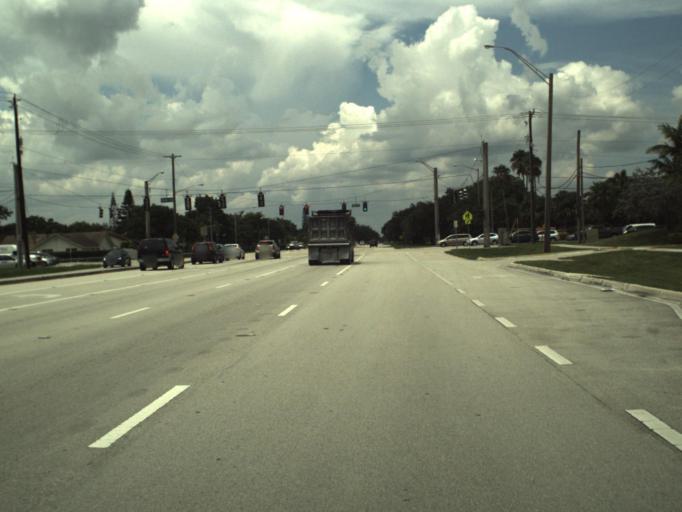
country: US
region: Florida
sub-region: Broward County
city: Cooper City
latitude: 26.0302
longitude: -80.2794
